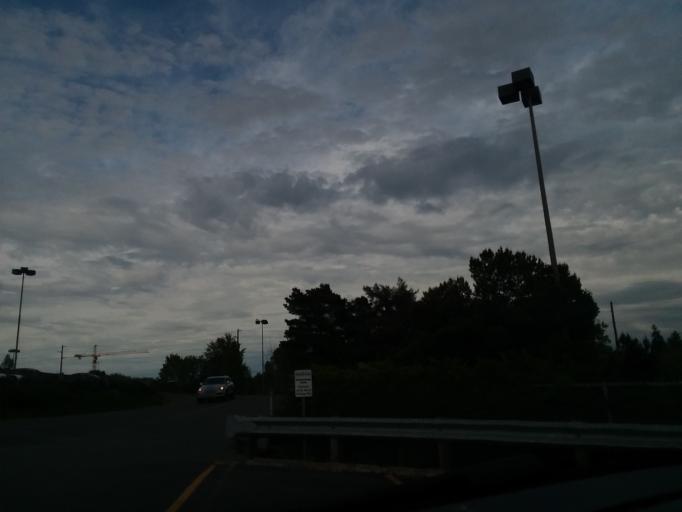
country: US
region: Washington
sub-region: King County
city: Shoreline
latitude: 47.7039
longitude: -122.3246
